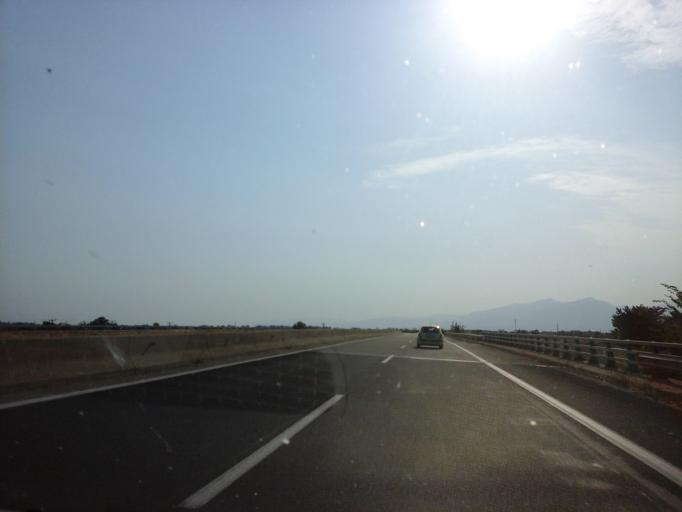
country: GR
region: East Macedonia and Thrace
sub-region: Nomos Xanthis
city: Selero
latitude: 41.1194
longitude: 25.0457
